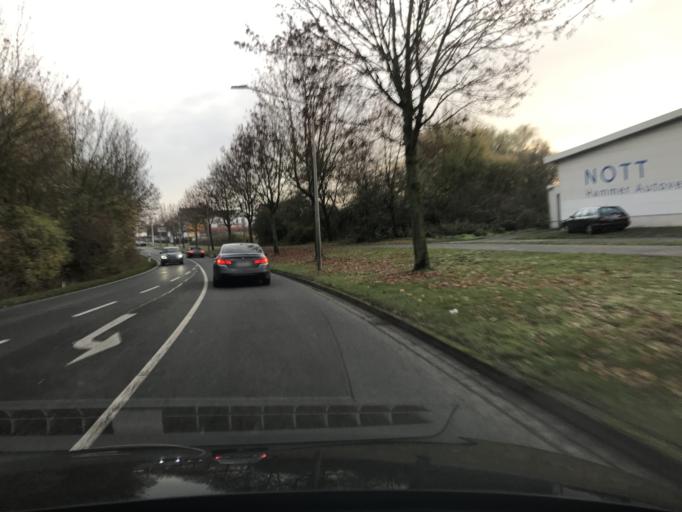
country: DE
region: North Rhine-Westphalia
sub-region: Regierungsbezirk Arnsberg
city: Hamm
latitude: 51.6969
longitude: 7.8207
